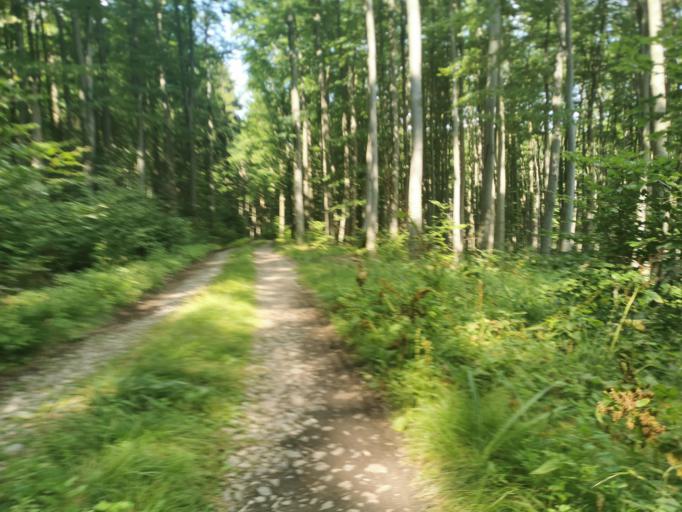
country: SK
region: Trenciansky
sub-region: Okres Myjava
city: Myjava
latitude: 48.8318
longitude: 17.5989
